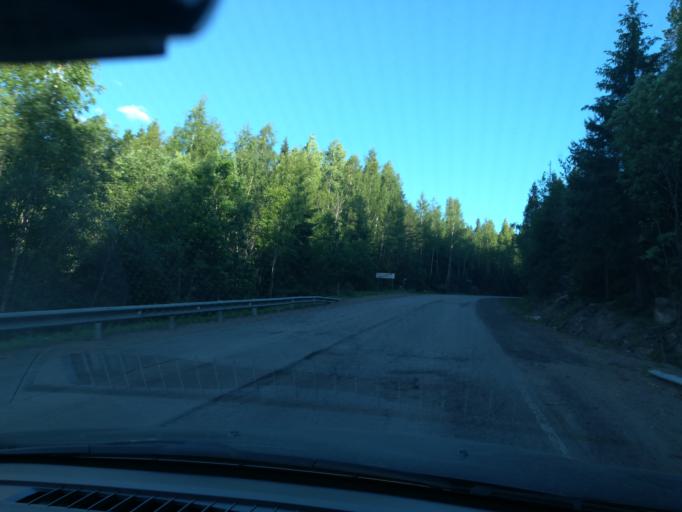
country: RU
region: Leningrad
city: Lesogorskiy
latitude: 61.0329
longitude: 28.9139
